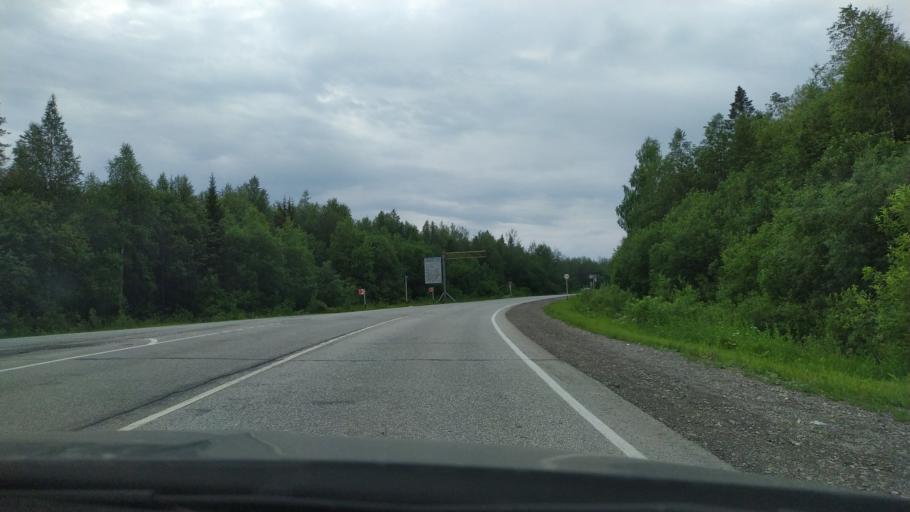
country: RU
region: Perm
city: Chusovoy
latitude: 58.3878
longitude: 57.9012
